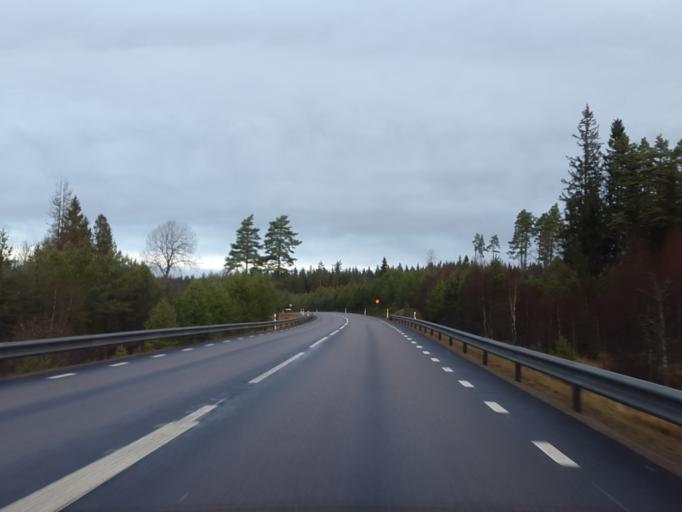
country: SE
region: Vaestra Goetaland
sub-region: Boras Kommun
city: Sandared
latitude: 57.7912
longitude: 12.7704
